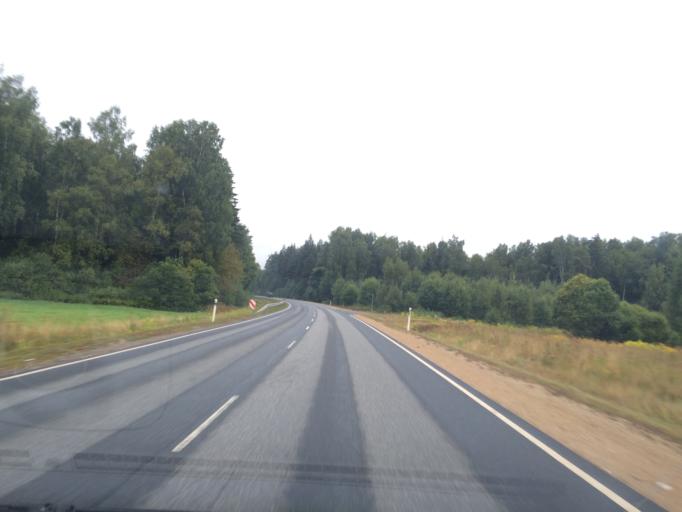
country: LV
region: Ogre
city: Ogre
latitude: 56.8583
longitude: 24.5896
